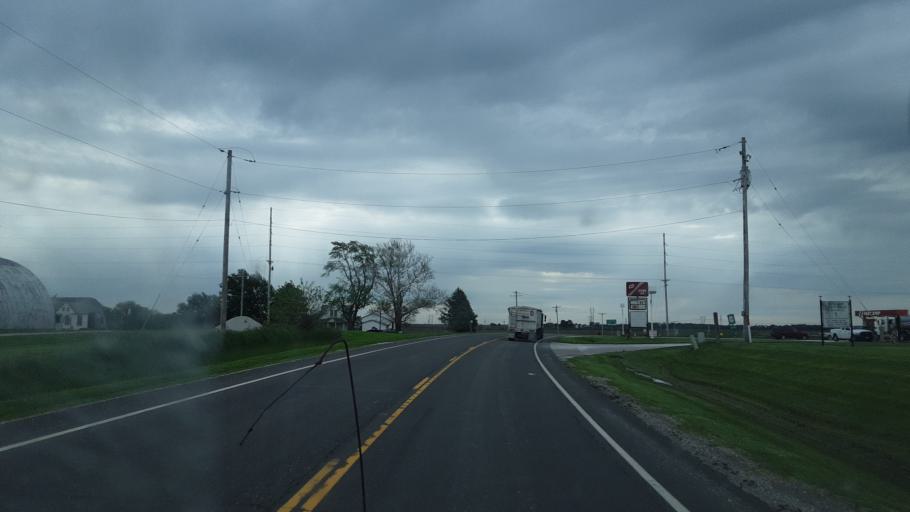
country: US
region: Illinois
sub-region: Fulton County
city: Astoria
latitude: 40.3514
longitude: -90.3158
